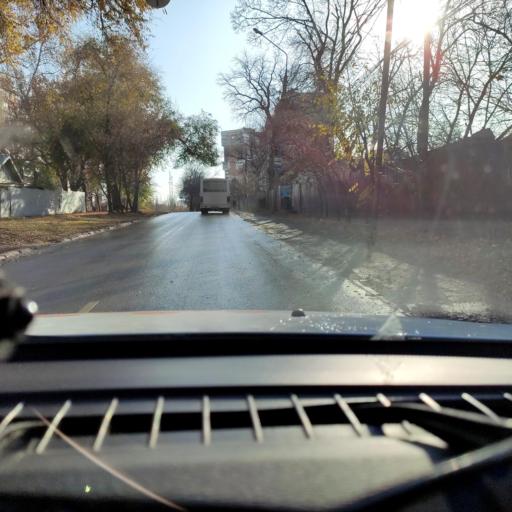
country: RU
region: Samara
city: Samara
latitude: 53.2411
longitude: 50.1769
